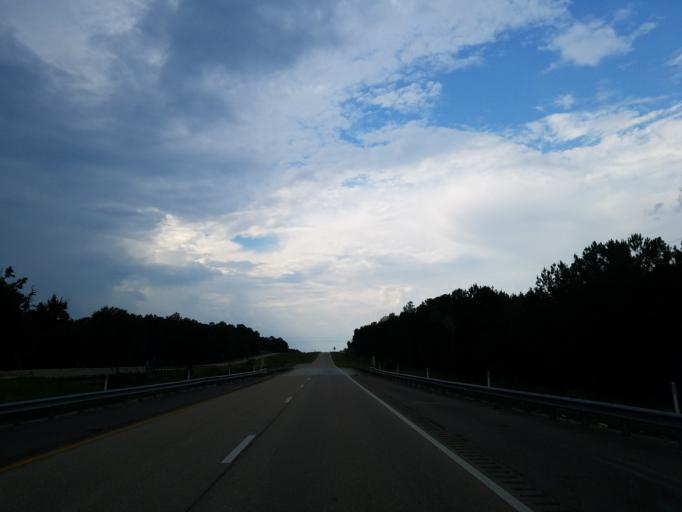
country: US
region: Mississippi
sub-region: Wayne County
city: Belmont
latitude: 31.4706
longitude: -88.4763
